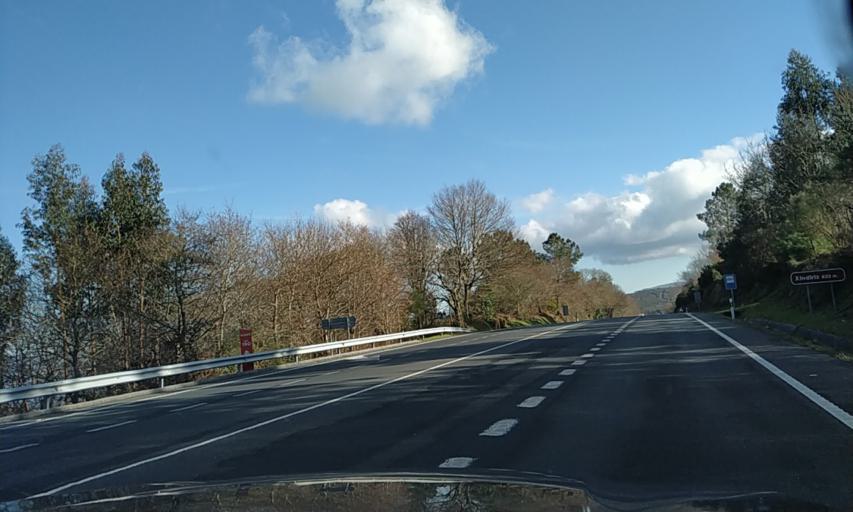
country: ES
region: Galicia
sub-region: Provincia de Pontevedra
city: Silleda
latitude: 42.7062
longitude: -8.3453
